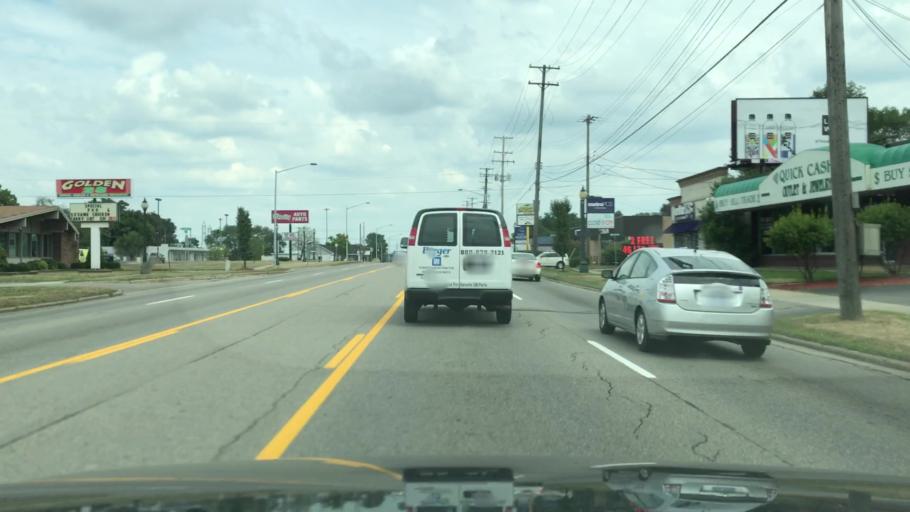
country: US
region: Michigan
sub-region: Kent County
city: Wyoming
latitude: 42.9132
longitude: -85.6826
